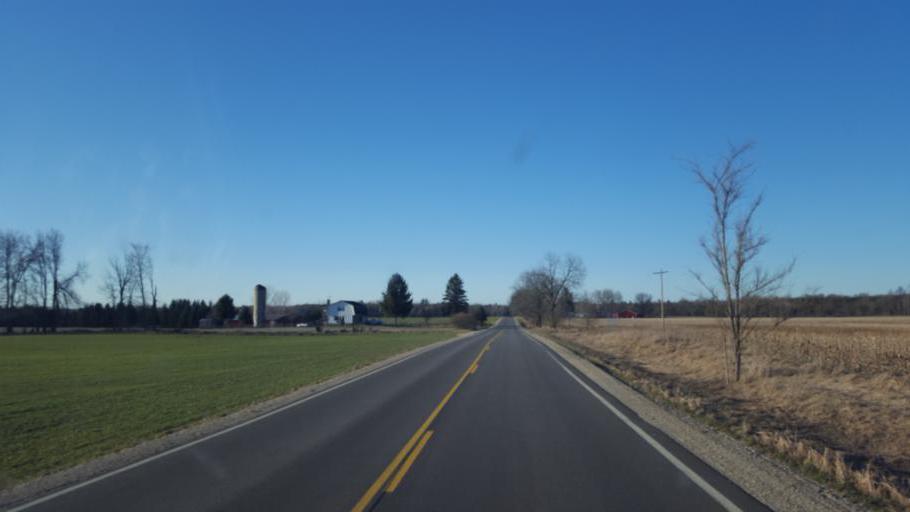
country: US
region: Michigan
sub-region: Mecosta County
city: Canadian Lakes
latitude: 43.5279
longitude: -85.2544
